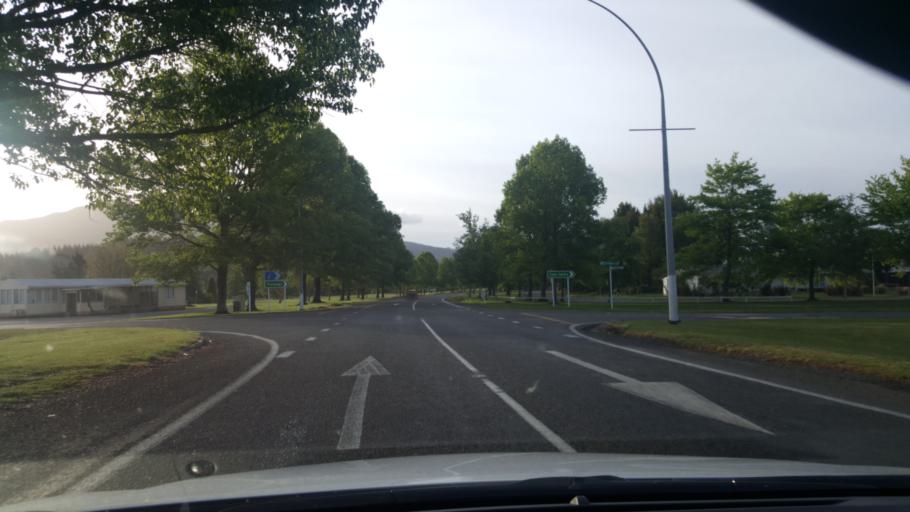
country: NZ
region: Waikato
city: Turangi
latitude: -38.9957
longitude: 175.8033
